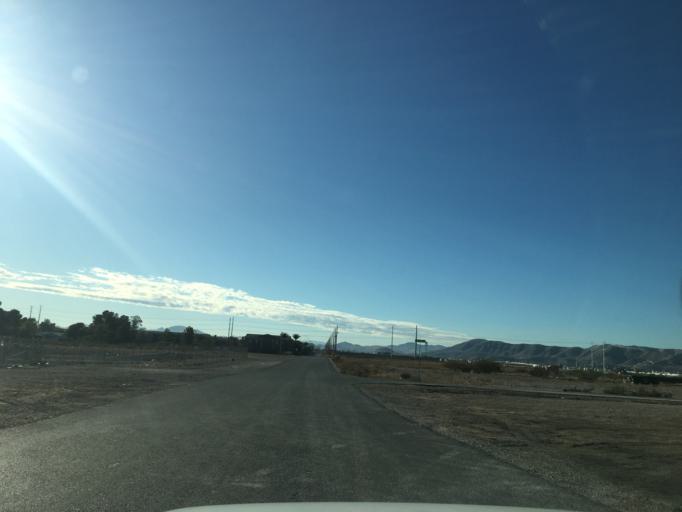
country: US
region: Nevada
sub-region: Clark County
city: Enterprise
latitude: 36.0088
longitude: -115.1702
